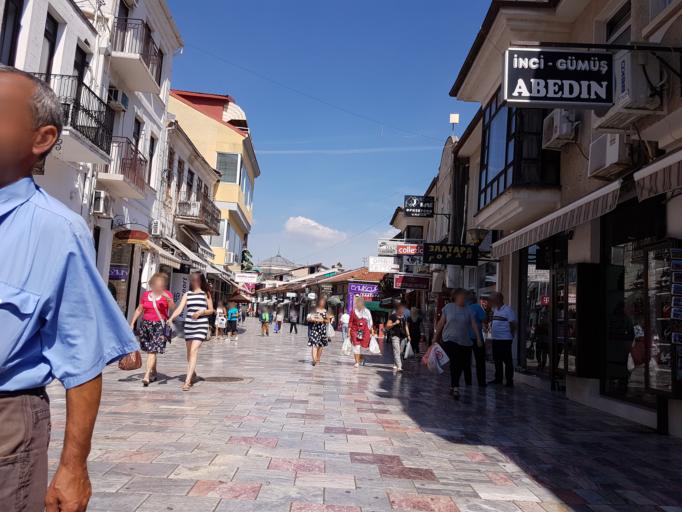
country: MK
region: Ohrid
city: Ohrid
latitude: 41.1142
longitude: 20.8001
